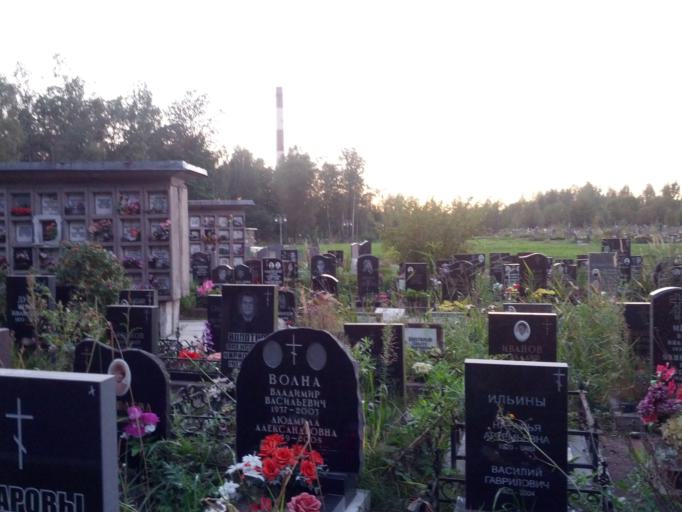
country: RU
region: St.-Petersburg
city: Obukhovo
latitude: 59.9125
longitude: 30.4320
